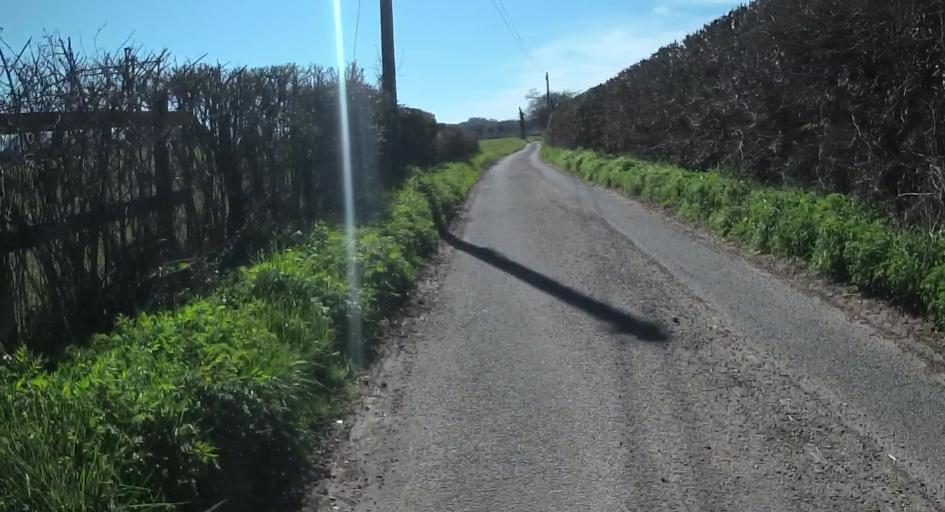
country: GB
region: England
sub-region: Hampshire
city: Old Basing
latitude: 51.2403
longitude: -1.0272
